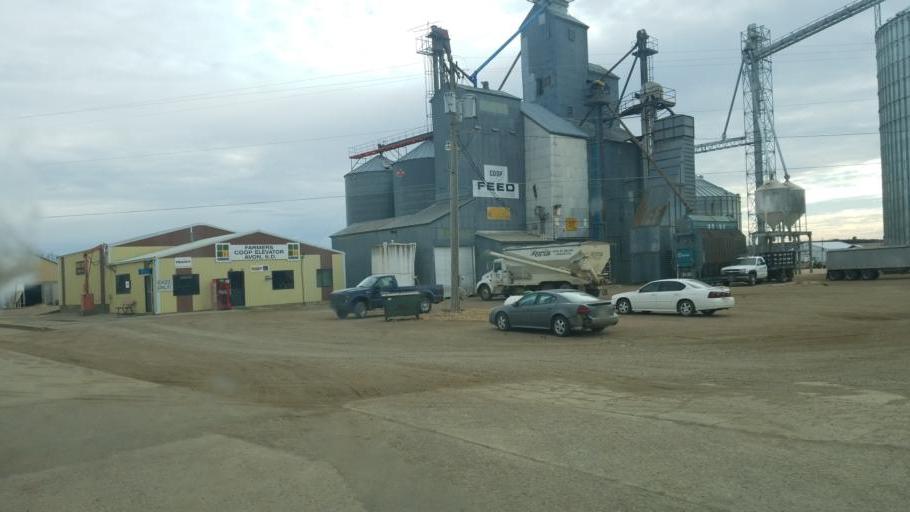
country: US
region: South Dakota
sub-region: Bon Homme County
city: Tyndall
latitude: 43.0037
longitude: -98.0601
